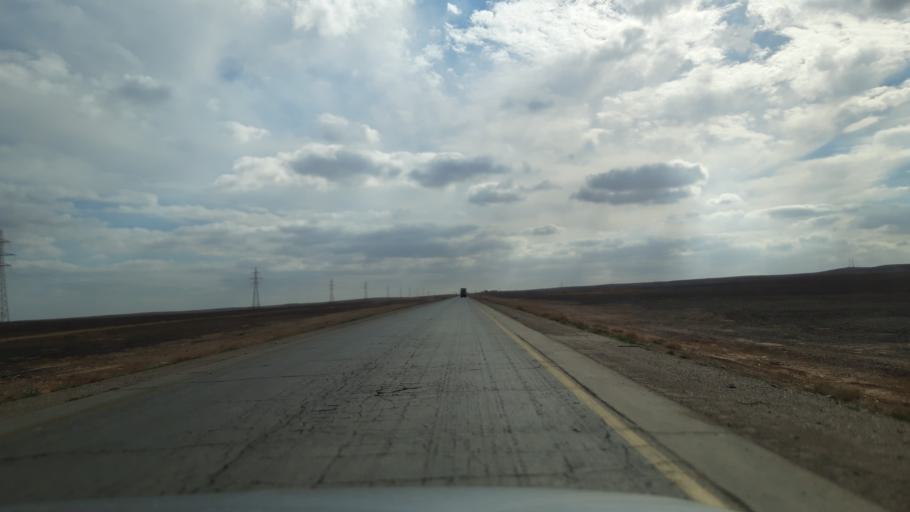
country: JO
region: Amman
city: Al Azraq ash Shamali
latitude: 31.7637
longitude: 36.5557
